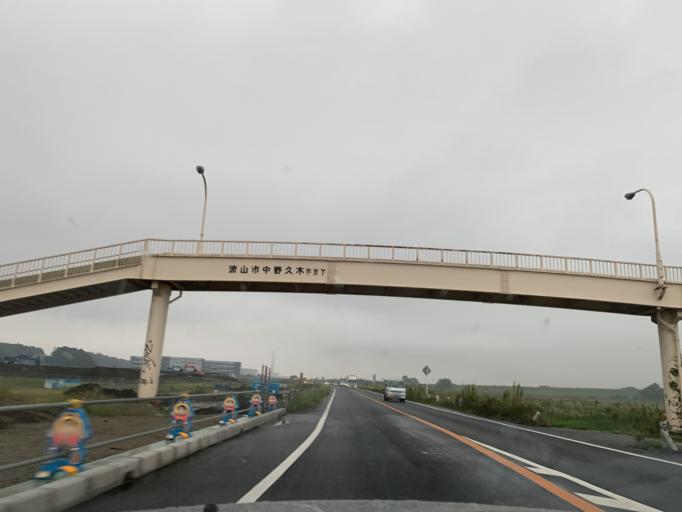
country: JP
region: Chiba
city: Nagareyama
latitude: 35.8958
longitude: 139.8928
